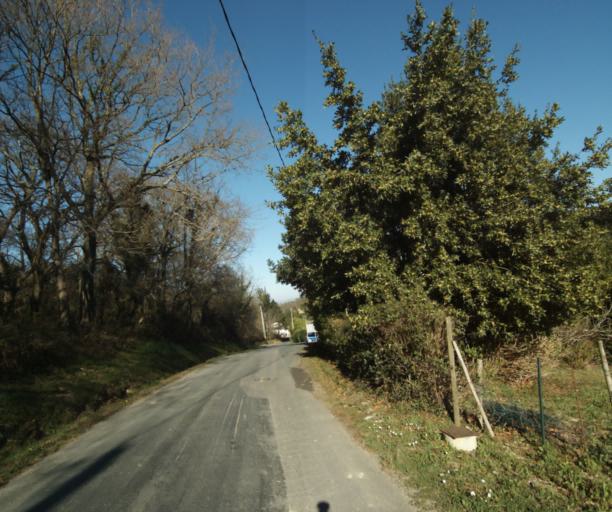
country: FR
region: Aquitaine
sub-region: Departement des Pyrenees-Atlantiques
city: Hendaye
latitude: 43.3573
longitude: -1.7401
